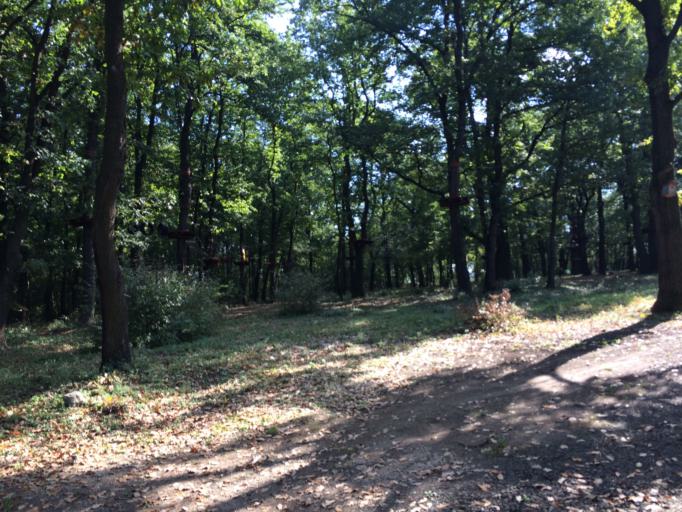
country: HU
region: Pest
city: Nagymaros
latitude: 47.8307
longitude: 18.9438
